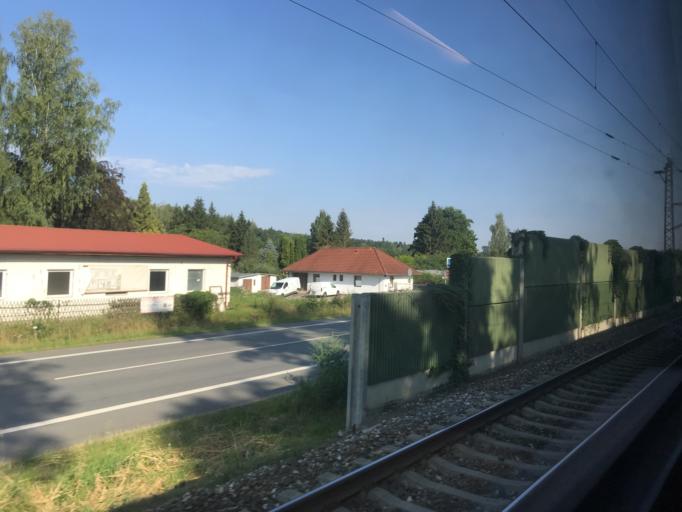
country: CZ
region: Jihocesky
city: Plana nad Luznici
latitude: 49.3439
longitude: 14.7105
